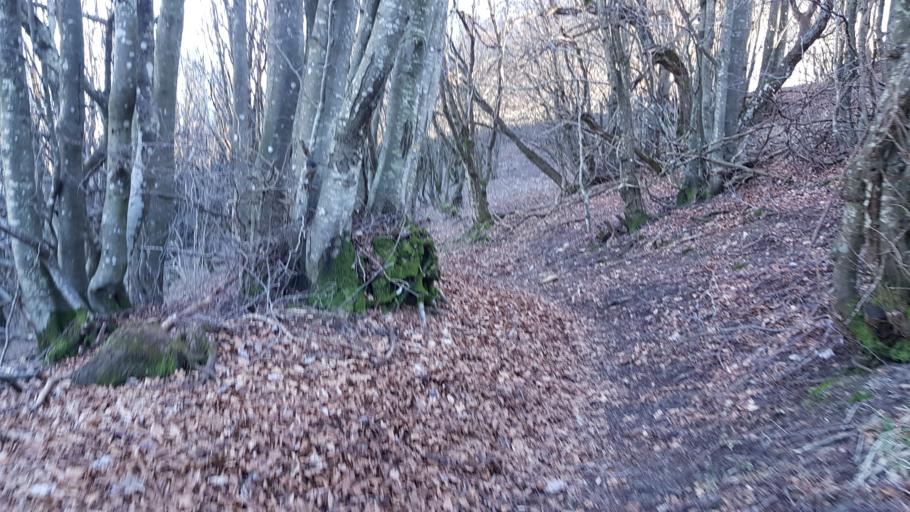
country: IT
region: Liguria
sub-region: Provincia di Genova
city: Torriglia
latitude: 44.5438
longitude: 9.1532
